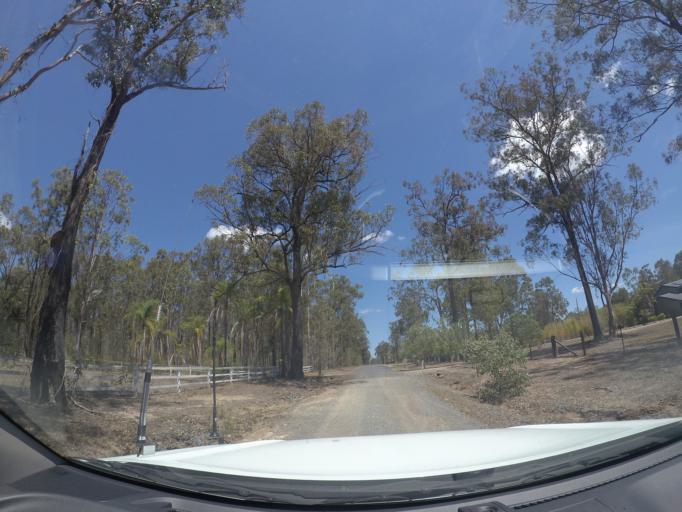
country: AU
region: Queensland
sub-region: Ipswich
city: Springfield Lakes
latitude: -27.6939
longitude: 152.9497
